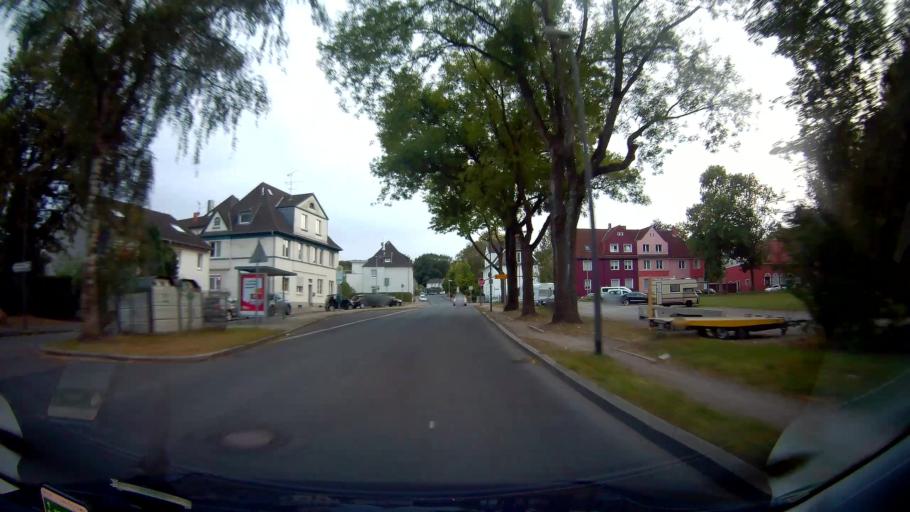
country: DE
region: North Rhine-Westphalia
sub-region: Regierungsbezirk Arnsberg
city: Herne
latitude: 51.5290
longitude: 7.2525
